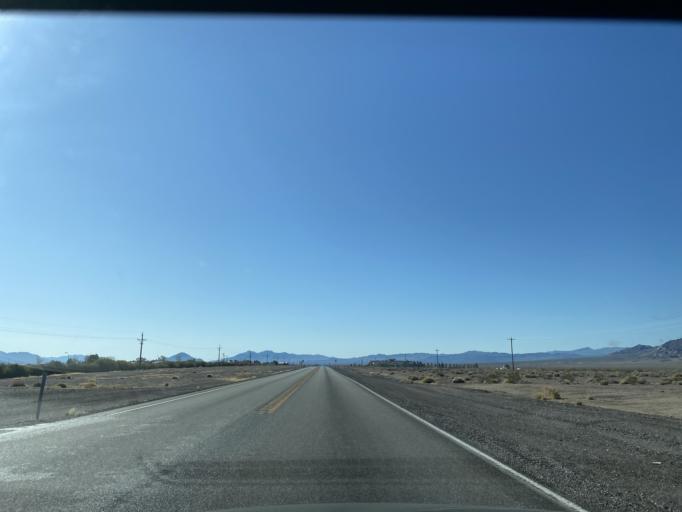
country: US
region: Nevada
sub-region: Nye County
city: Pahrump
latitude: 36.4216
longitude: -116.4222
